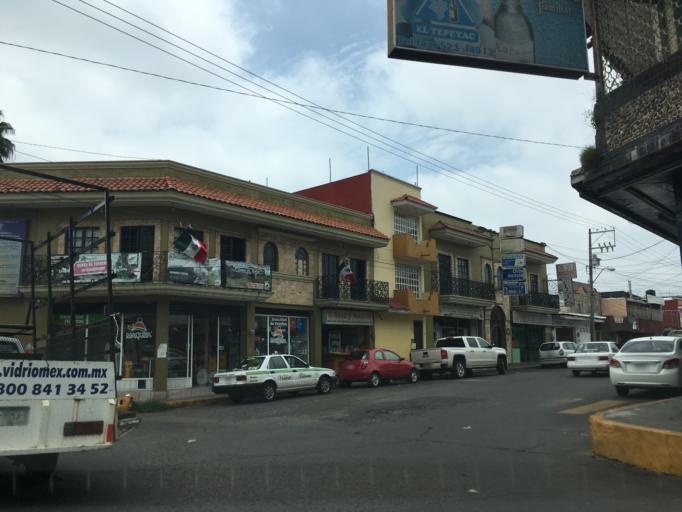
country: MX
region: Michoacan
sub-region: Uruapan
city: Uruapan
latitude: 19.4202
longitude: -102.0522
